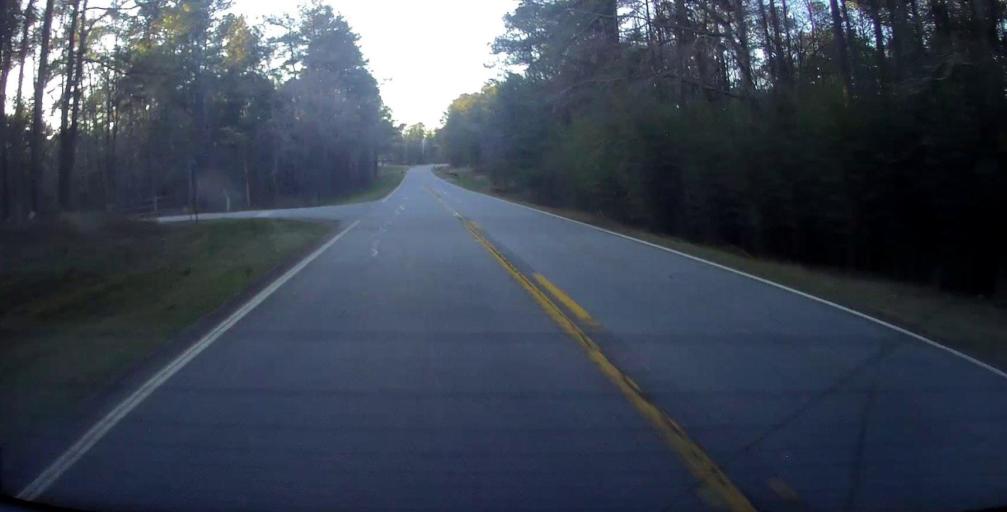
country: US
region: Alabama
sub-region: Lee County
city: Smiths Station
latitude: 32.6217
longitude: -85.0318
